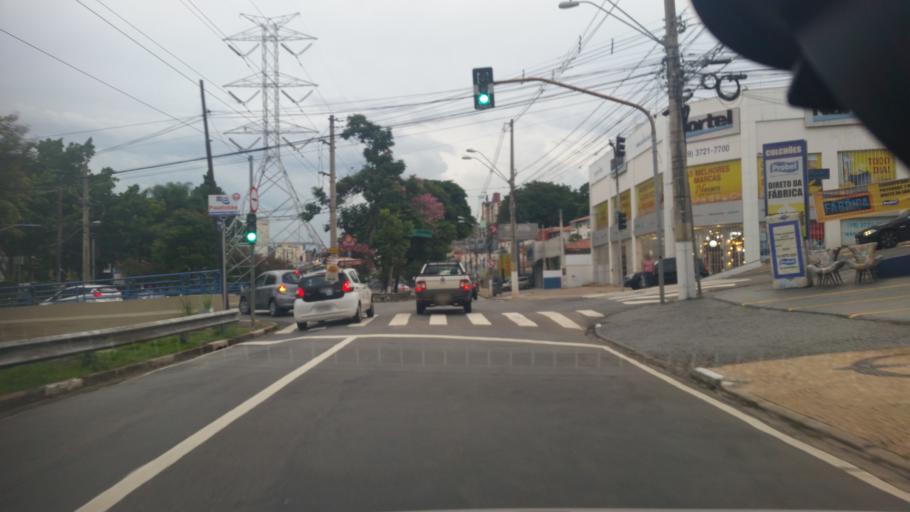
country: BR
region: Sao Paulo
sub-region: Campinas
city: Campinas
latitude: -22.8881
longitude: -47.0544
